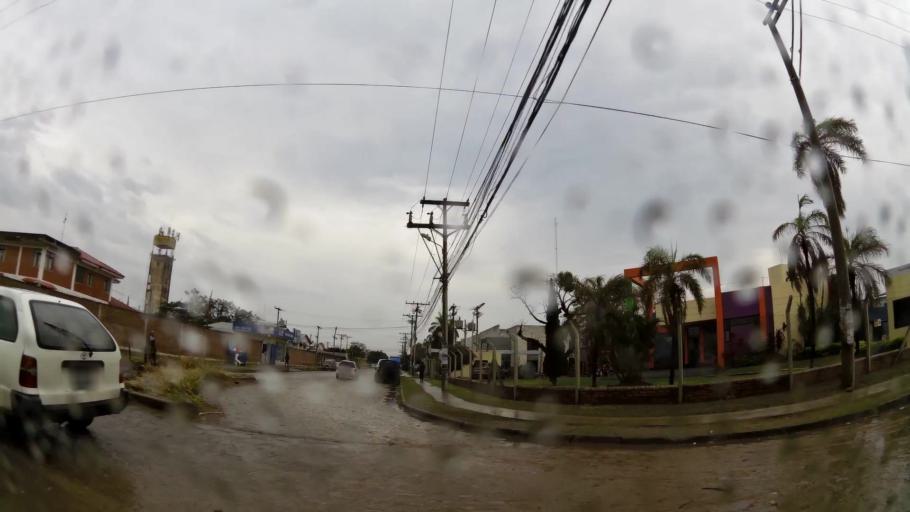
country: BO
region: Santa Cruz
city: Santa Cruz de la Sierra
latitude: -17.7666
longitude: -63.1437
